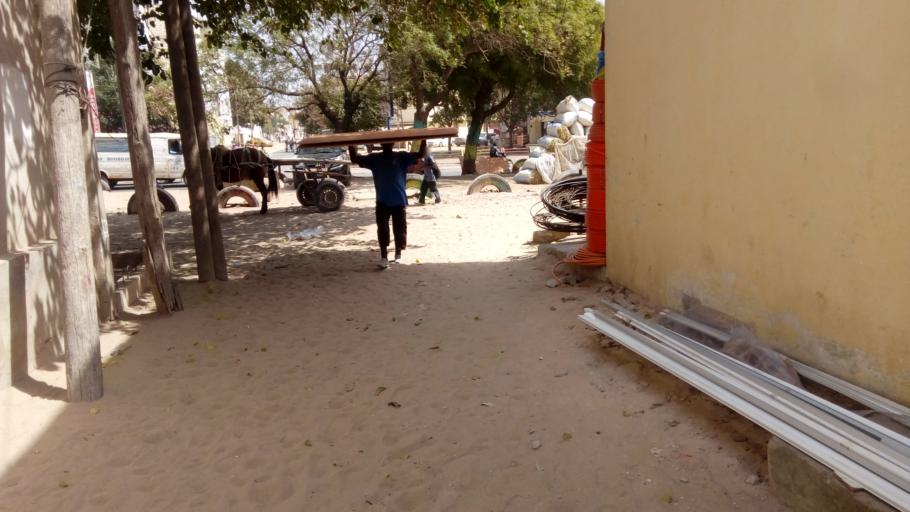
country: SN
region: Dakar
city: Grand Dakar
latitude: 14.7130
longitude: -17.4467
